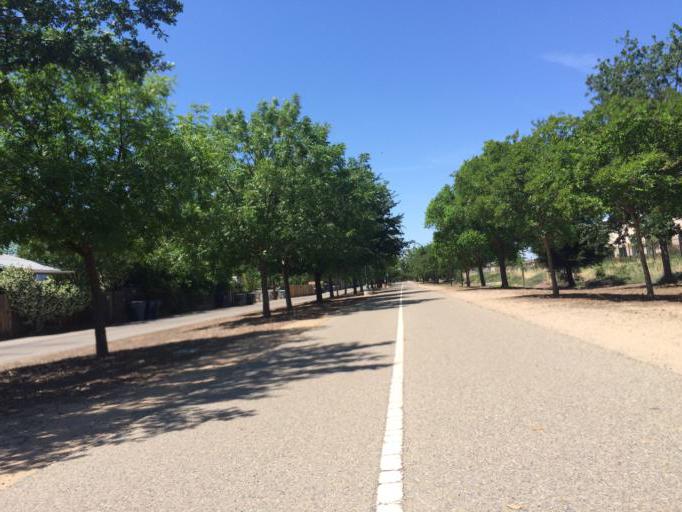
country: US
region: California
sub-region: Fresno County
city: Clovis
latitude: 36.8317
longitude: -119.7018
